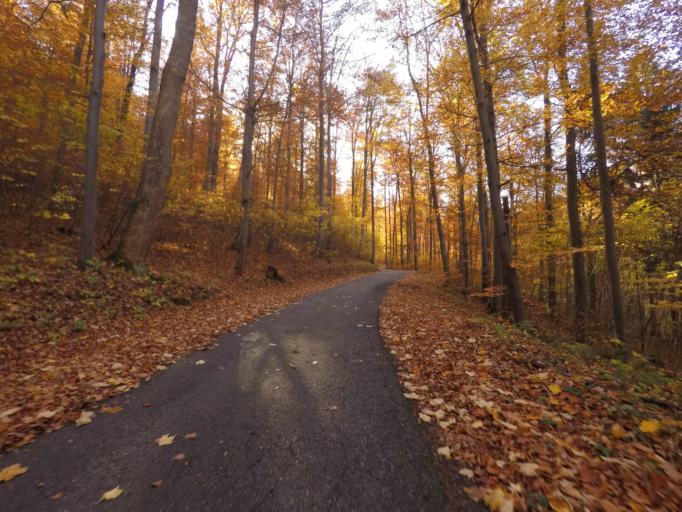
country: DE
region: Baden-Wuerttemberg
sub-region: Tuebingen Region
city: Pfullingen
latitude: 48.4407
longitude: 9.2379
